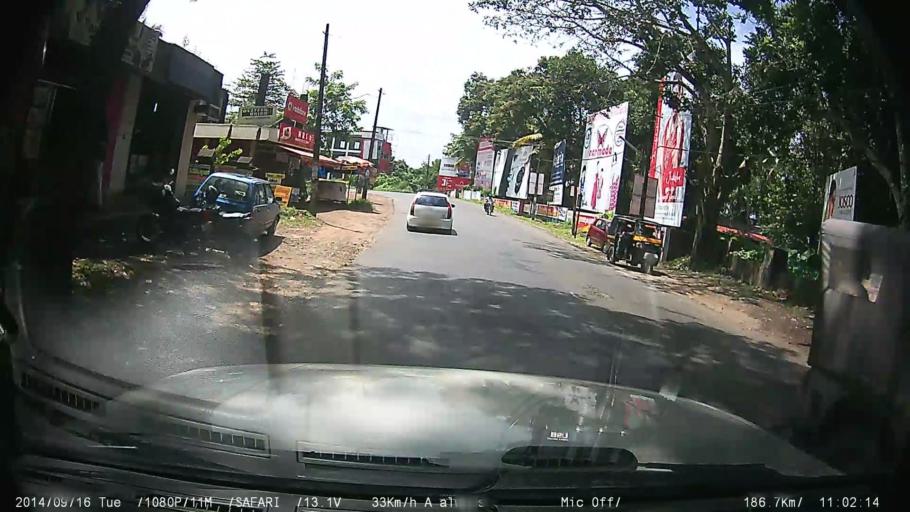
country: IN
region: Kerala
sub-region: Kottayam
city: Kottayam
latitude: 9.5522
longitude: 76.5130
